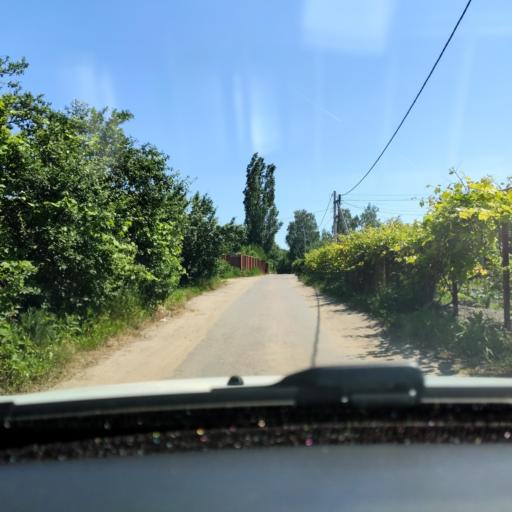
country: RU
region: Voronezj
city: Shilovo
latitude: 51.5921
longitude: 39.1468
